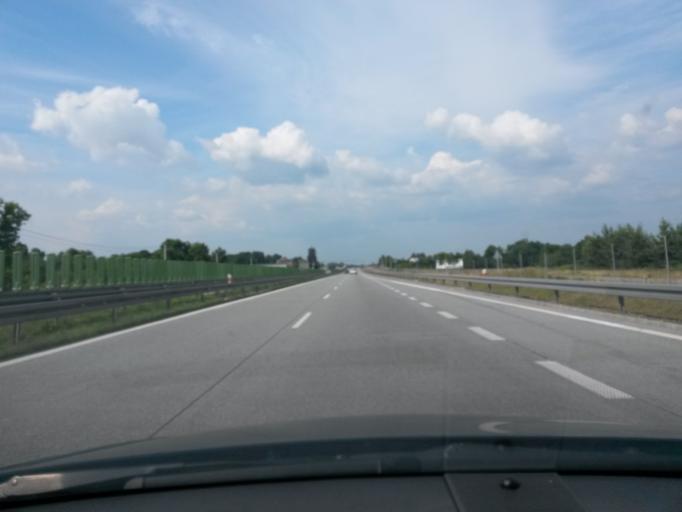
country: PL
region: Lodz Voivodeship
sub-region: Powiat rawski
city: Rawa Mazowiecka
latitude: 51.7379
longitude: 20.2332
